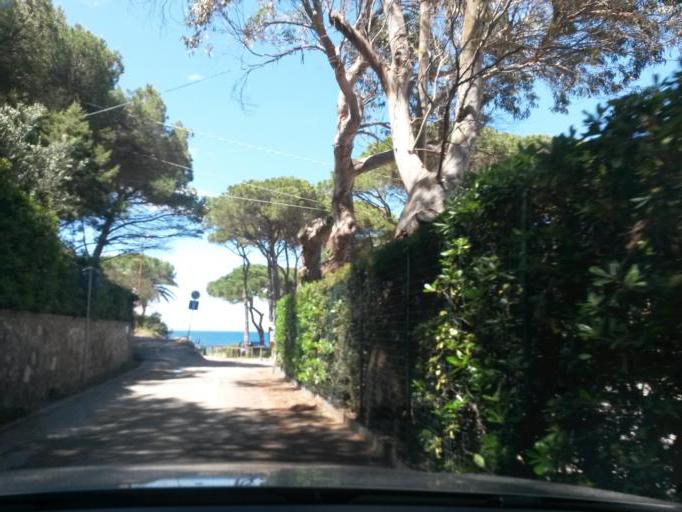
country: IT
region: Tuscany
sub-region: Provincia di Livorno
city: Rio Marina
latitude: 42.8659
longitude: 10.4196
